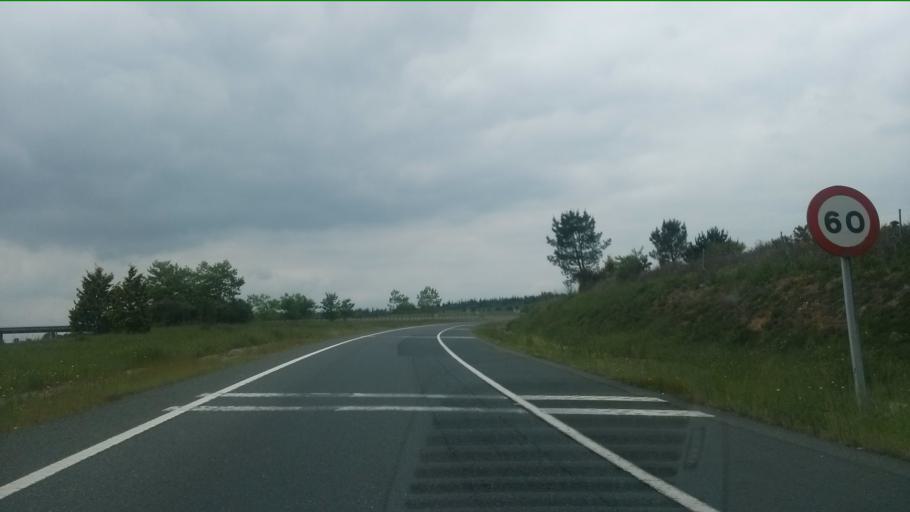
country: ES
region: Galicia
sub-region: Provincia de Lugo
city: Guitiriz
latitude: 43.1934
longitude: -7.9507
